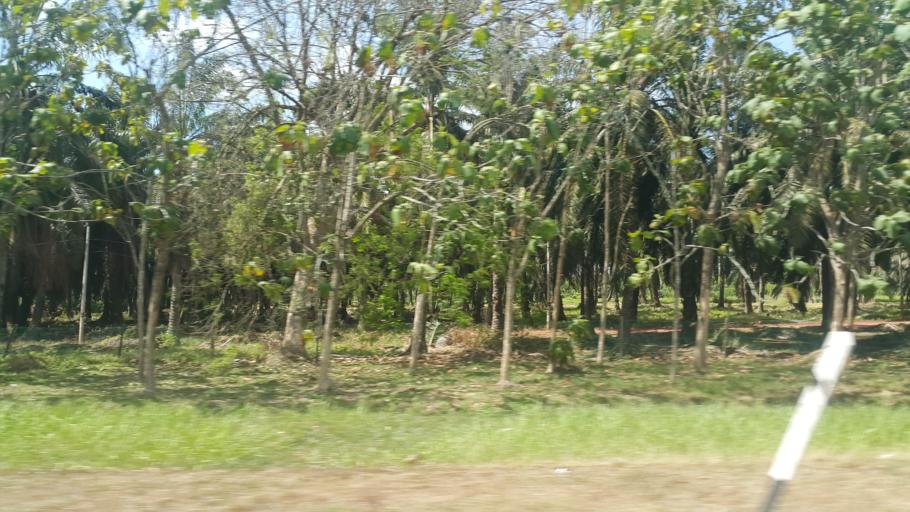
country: MY
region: Johor
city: Bakri
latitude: 2.1608
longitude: 102.6550
